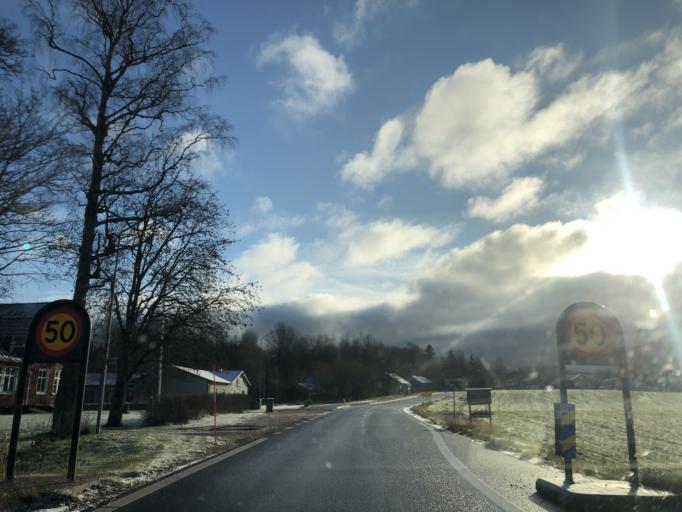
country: SE
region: Vaestra Goetaland
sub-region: Tranemo Kommun
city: Limmared
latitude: 57.6237
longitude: 13.4617
